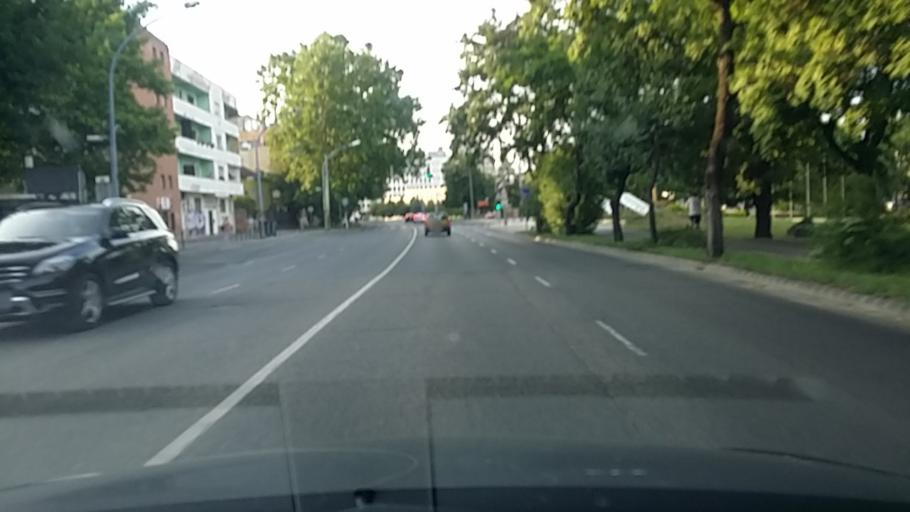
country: HU
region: Borsod-Abauj-Zemplen
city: Miskolc
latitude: 48.0956
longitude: 20.7857
